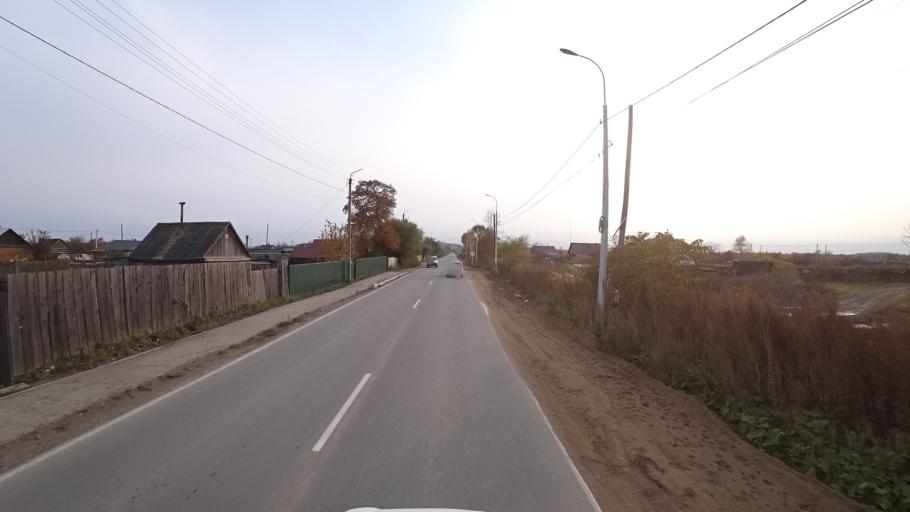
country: RU
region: Khabarovsk Krai
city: Amursk
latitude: 50.0887
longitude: 136.5012
